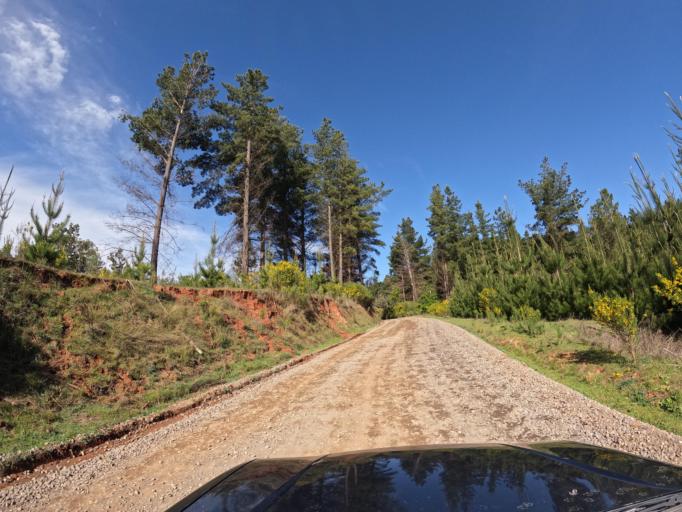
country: CL
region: Biobio
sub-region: Provincia de Biobio
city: La Laja
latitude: -37.0904
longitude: -72.8288
